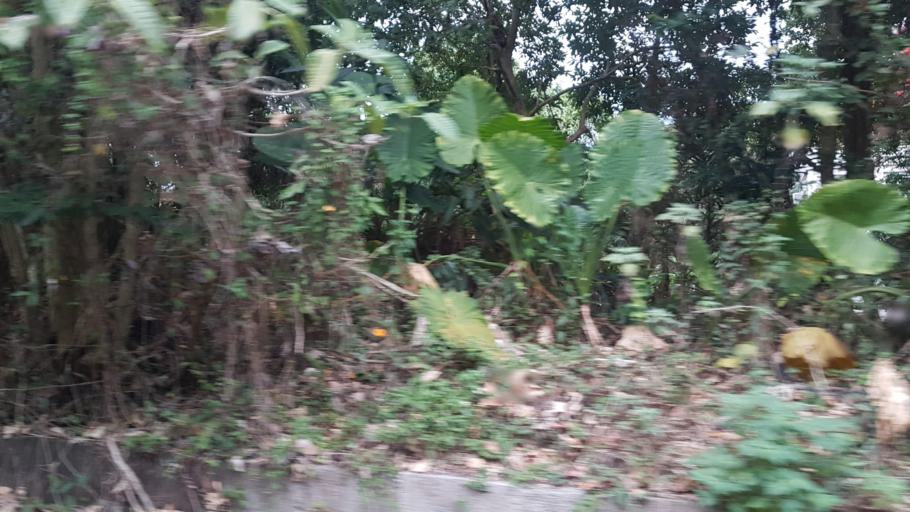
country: TW
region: Taiwan
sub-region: Chiayi
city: Jiayi Shi
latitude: 23.3268
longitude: 120.4867
